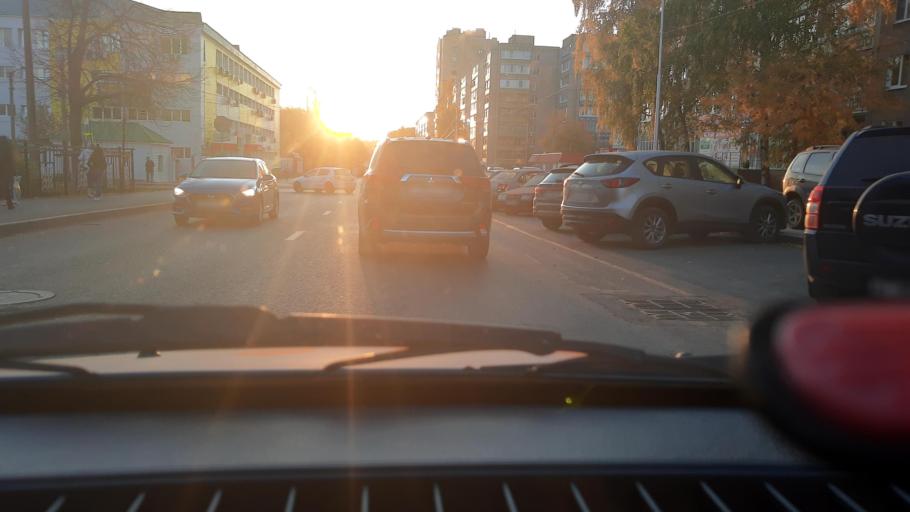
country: RU
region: Bashkortostan
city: Ufa
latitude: 54.7086
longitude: 56.0020
